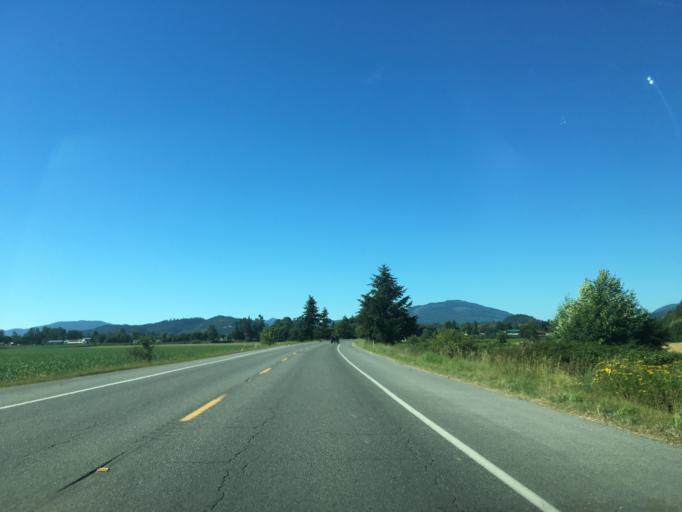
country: US
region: Washington
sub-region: Skagit County
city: Sedro-Woolley
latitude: 48.4893
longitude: -122.2457
